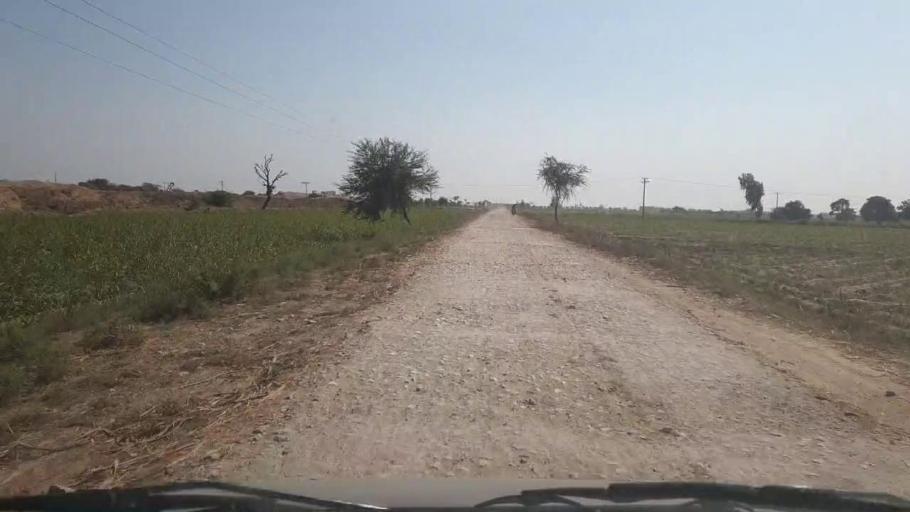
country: PK
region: Sindh
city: Samaro
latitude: 25.2532
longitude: 69.3546
